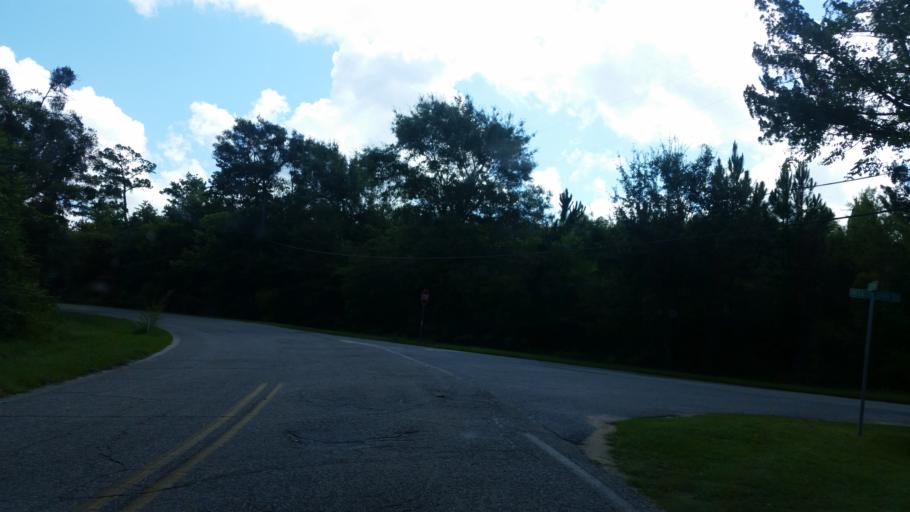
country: US
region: Florida
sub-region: Santa Rosa County
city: Bagdad
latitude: 30.6133
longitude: -87.0414
